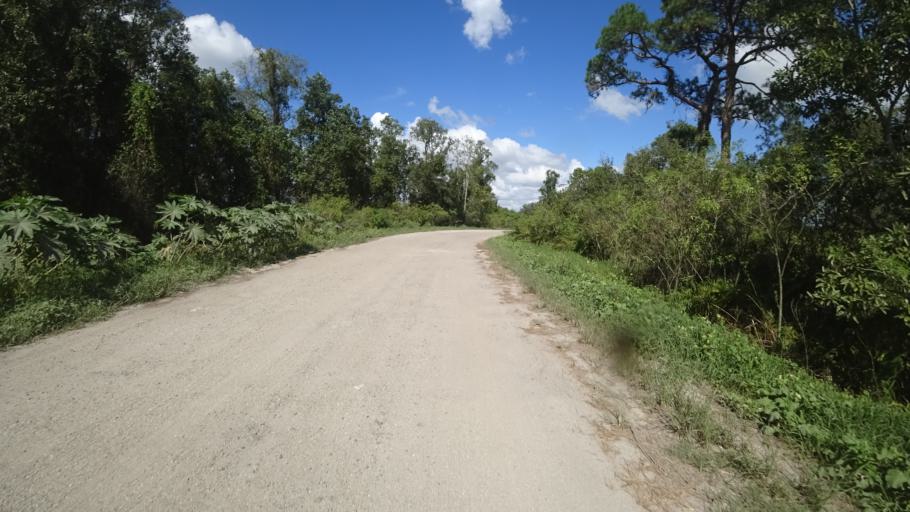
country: US
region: Florida
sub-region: DeSoto County
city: Arcadia
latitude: 27.3218
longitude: -82.1305
